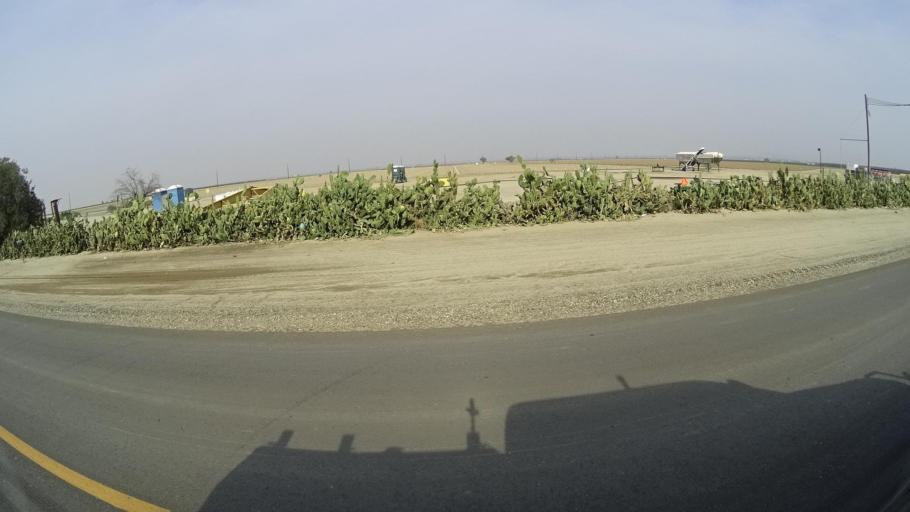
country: US
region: California
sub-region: Kern County
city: Arvin
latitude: 35.0454
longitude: -118.9097
